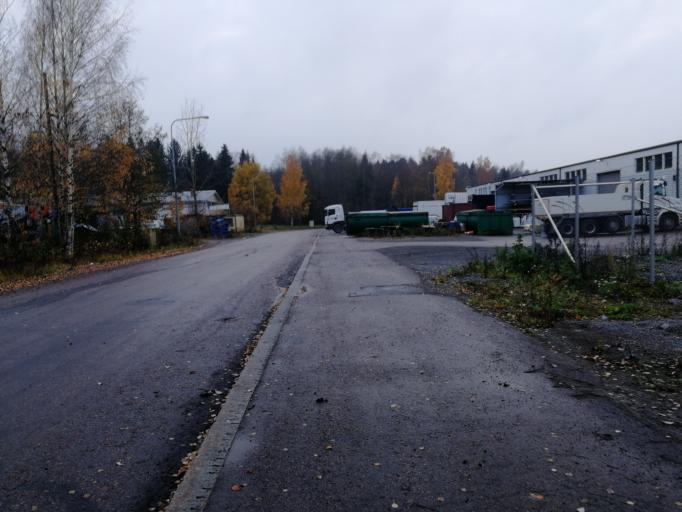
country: FI
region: Pirkanmaa
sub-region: Tampere
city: Tampere
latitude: 61.4480
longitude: 23.8960
